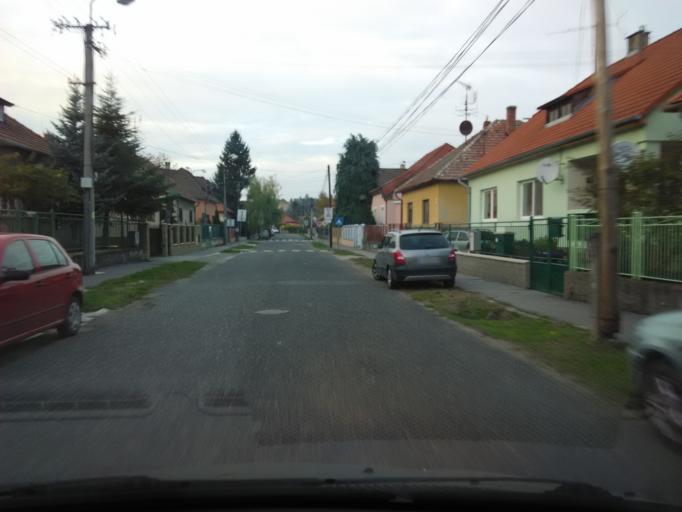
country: SK
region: Nitriansky
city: Levice
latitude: 48.2149
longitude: 18.6162
